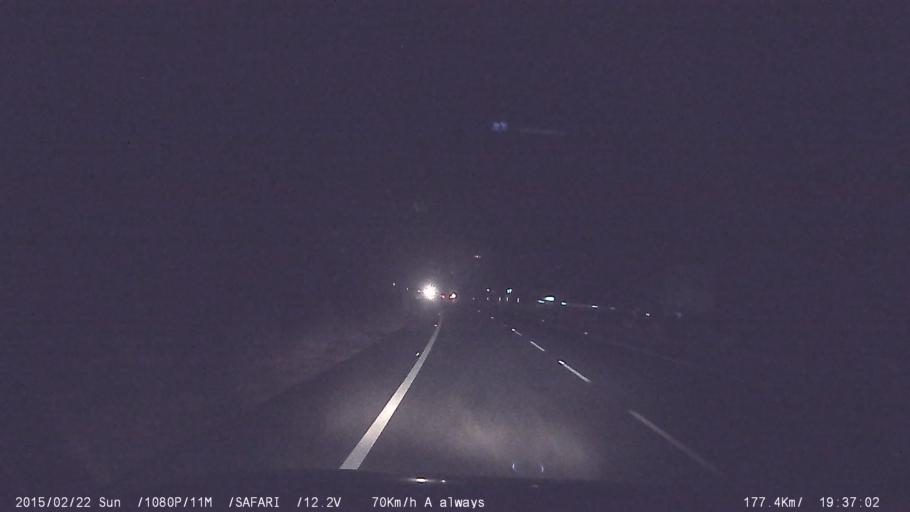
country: IN
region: Tamil Nadu
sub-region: Theni
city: Devadanappatti
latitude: 10.1341
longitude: 77.6204
